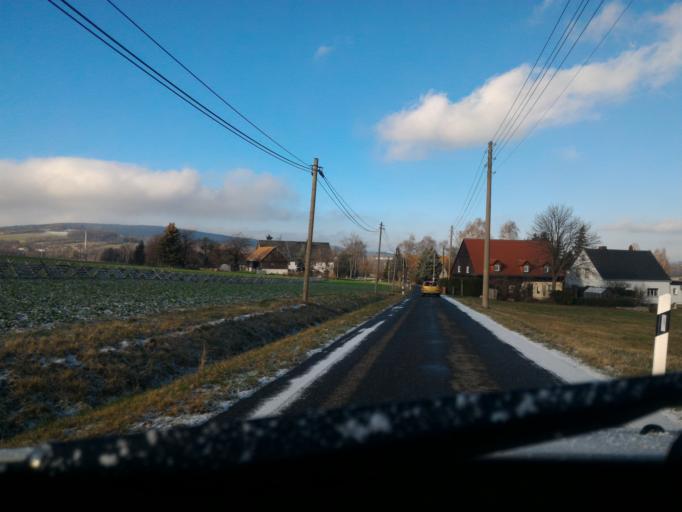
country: CZ
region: Ustecky
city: Varnsdorf
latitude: 50.8776
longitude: 14.6395
